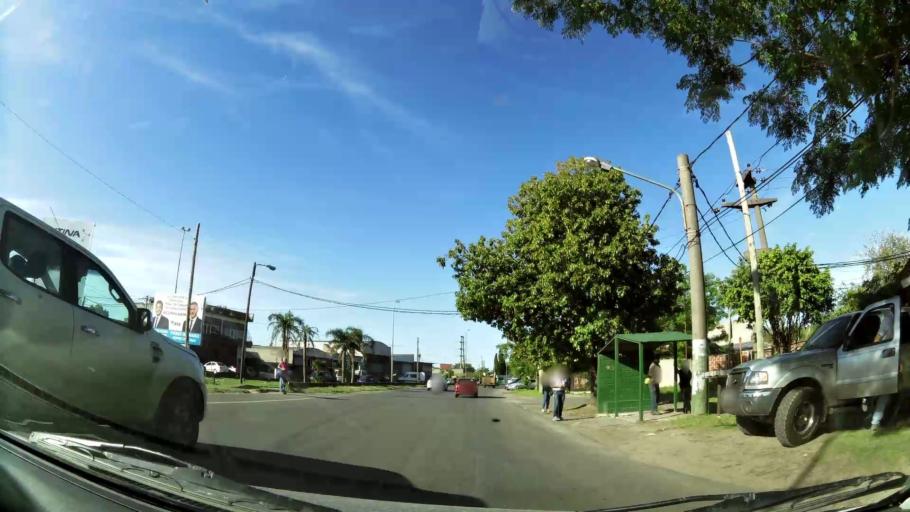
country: AR
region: Buenos Aires
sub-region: Partido de Almirante Brown
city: Adrogue
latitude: -34.8107
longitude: -58.3461
